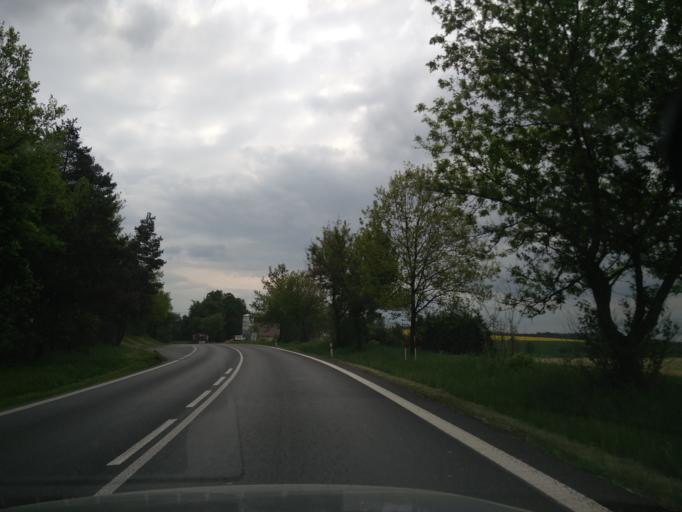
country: CZ
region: Central Bohemia
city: Milin
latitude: 49.5850
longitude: 14.0710
